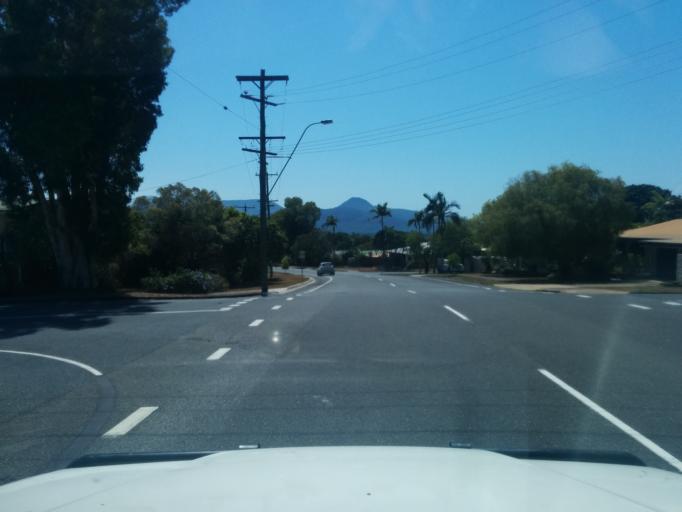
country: AU
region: Queensland
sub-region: Cairns
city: Woree
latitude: -16.9592
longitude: 145.7264
